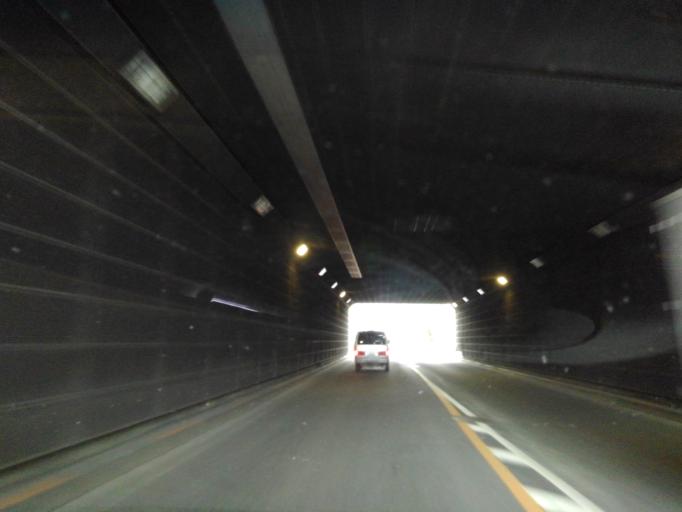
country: JP
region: Tokyo
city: Kokubunji
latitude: 35.6987
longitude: 139.4979
